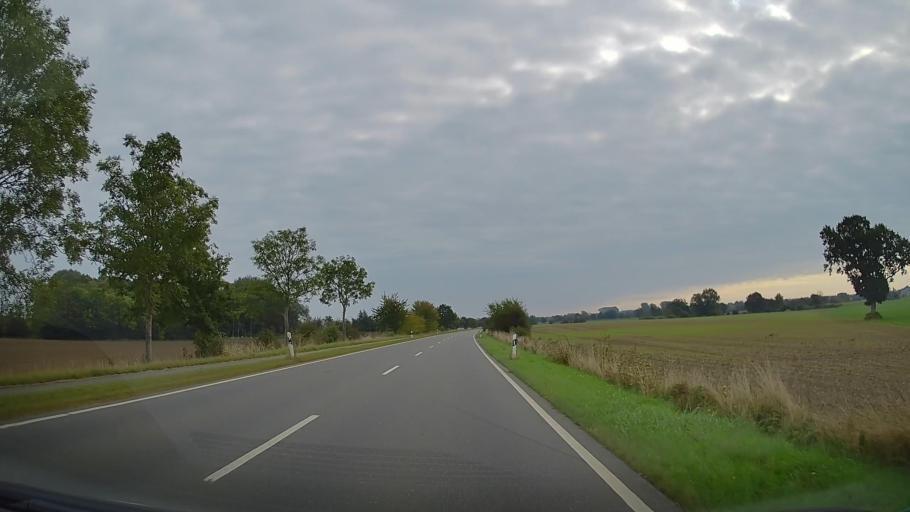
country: DE
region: Schleswig-Holstein
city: Krummbek
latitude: 54.3991
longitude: 10.4109
